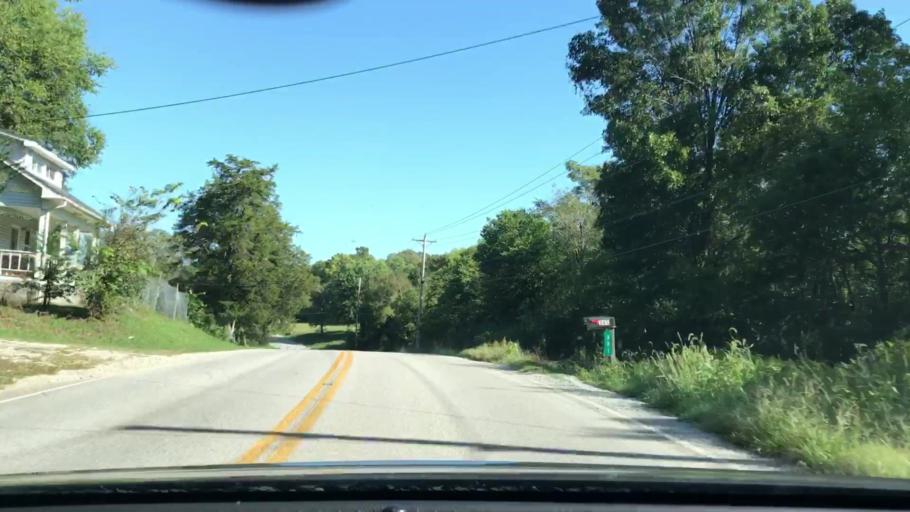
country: US
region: Tennessee
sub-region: Smith County
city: Carthage
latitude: 36.3221
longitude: -85.9070
